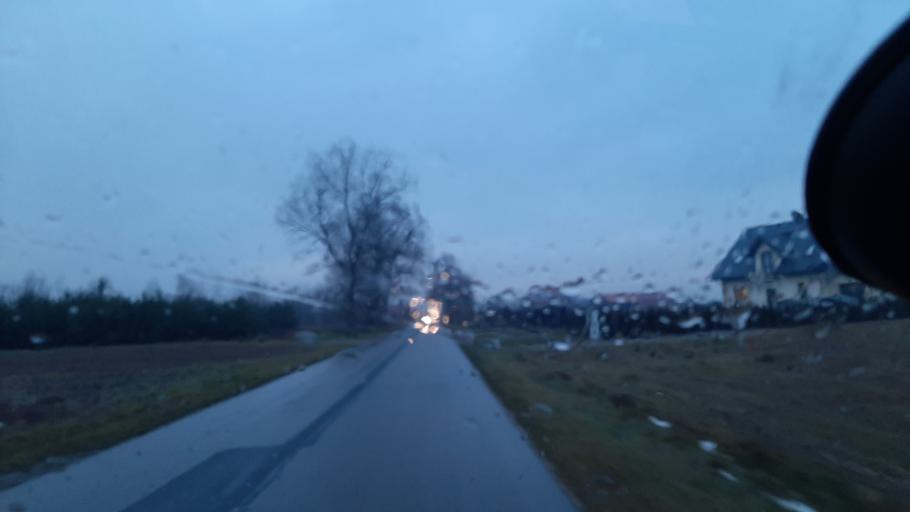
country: PL
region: Lublin Voivodeship
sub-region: Powiat lubartowski
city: Ostrowek
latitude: 51.5397
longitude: 22.5704
